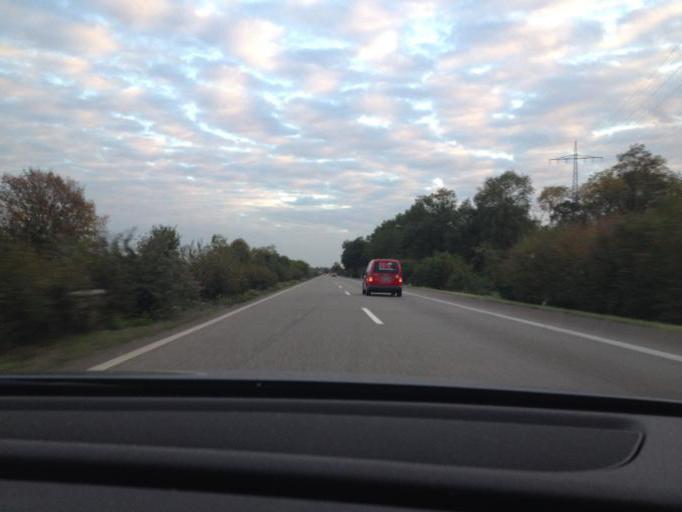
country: DE
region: Rheinland-Pfalz
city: Waldsee
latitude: 49.3766
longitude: 8.4202
